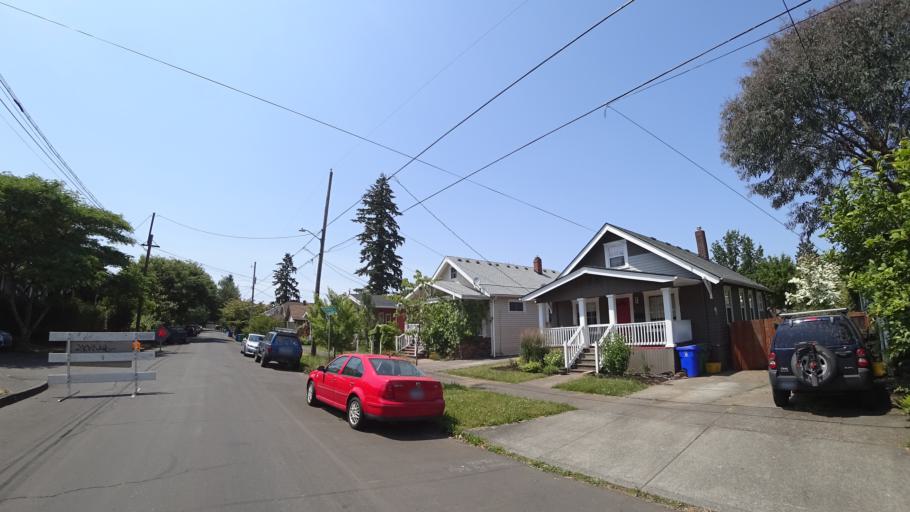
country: US
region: Oregon
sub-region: Multnomah County
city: Portland
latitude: 45.5803
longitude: -122.6899
